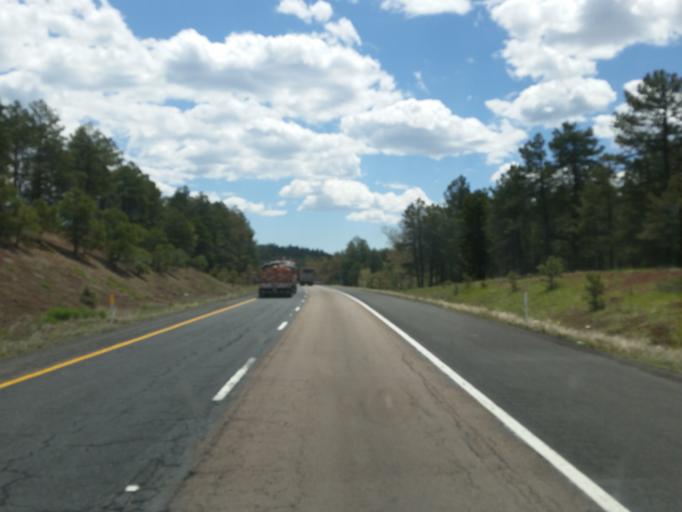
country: US
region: Arizona
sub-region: Coconino County
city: Parks
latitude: 35.2528
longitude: -111.9107
